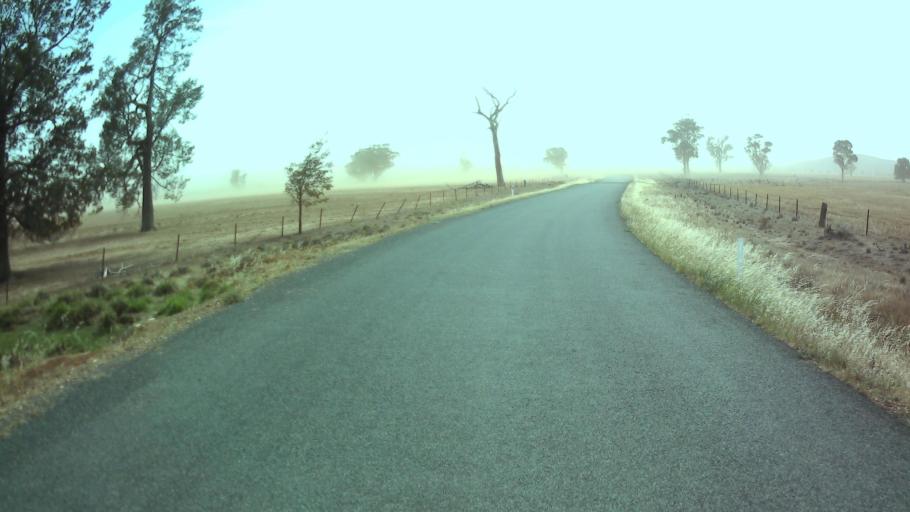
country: AU
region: New South Wales
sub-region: Weddin
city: Grenfell
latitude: -33.7371
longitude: 147.9940
